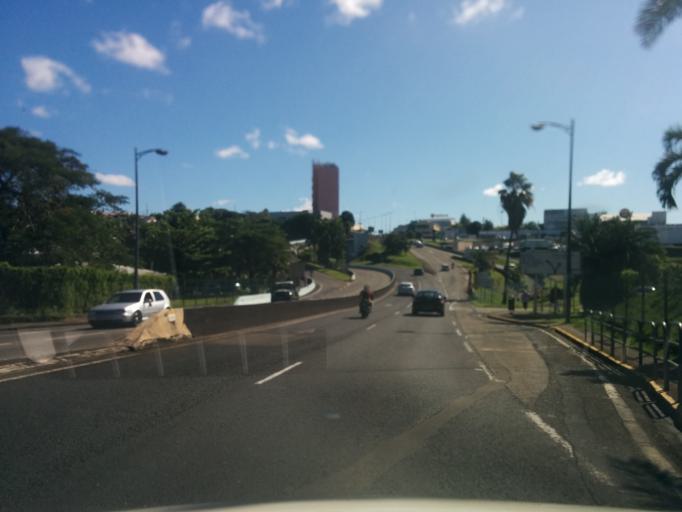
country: MQ
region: Martinique
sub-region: Martinique
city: Fort-de-France
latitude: 14.6055
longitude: -61.0903
